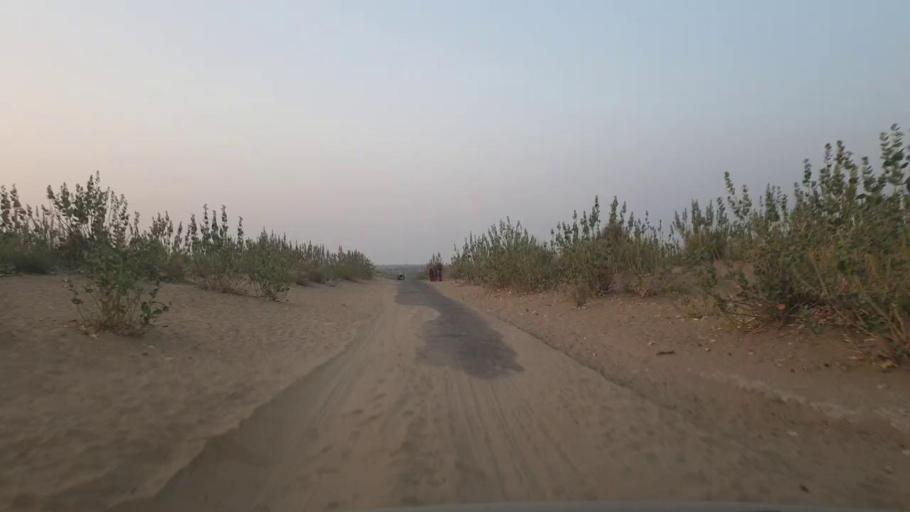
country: PK
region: Sindh
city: Umarkot
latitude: 25.2941
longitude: 70.0765
